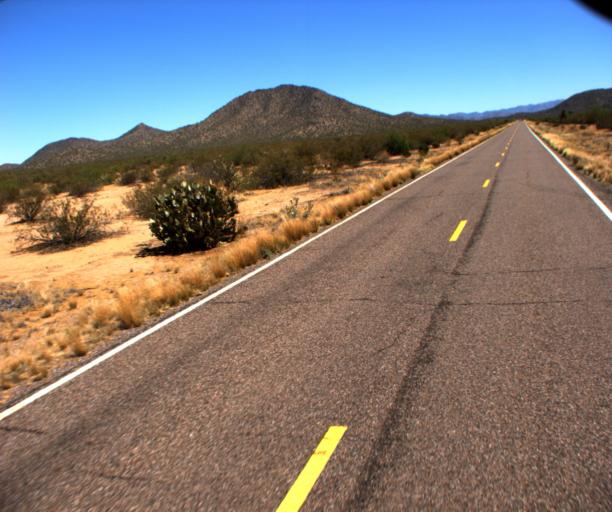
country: US
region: Arizona
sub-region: Yavapai County
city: Congress
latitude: 34.0841
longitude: -113.0160
